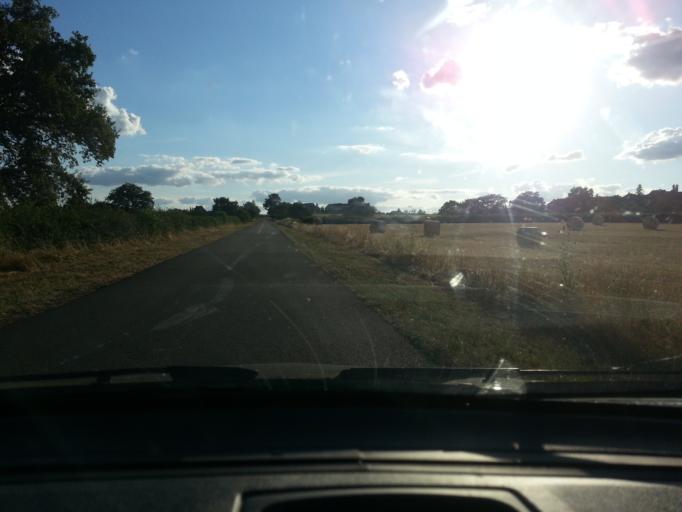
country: FR
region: Bourgogne
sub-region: Departement de Saone-et-Loire
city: Buxy
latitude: 46.7442
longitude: 4.6403
